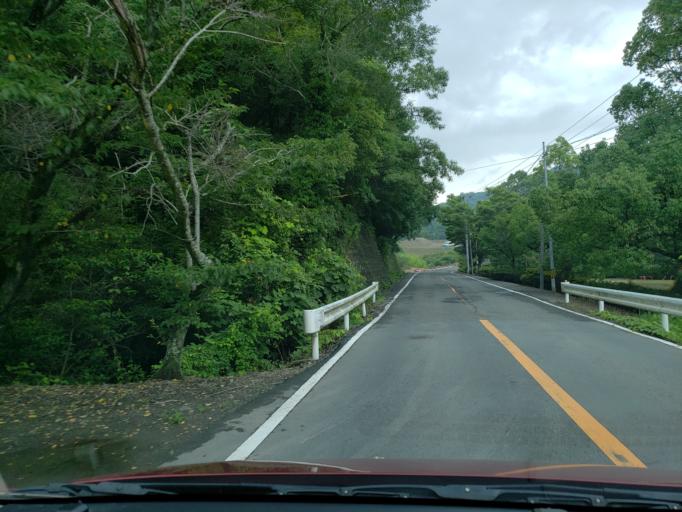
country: JP
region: Tokushima
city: Kamojimacho-jogejima
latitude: 34.1126
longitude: 134.2956
